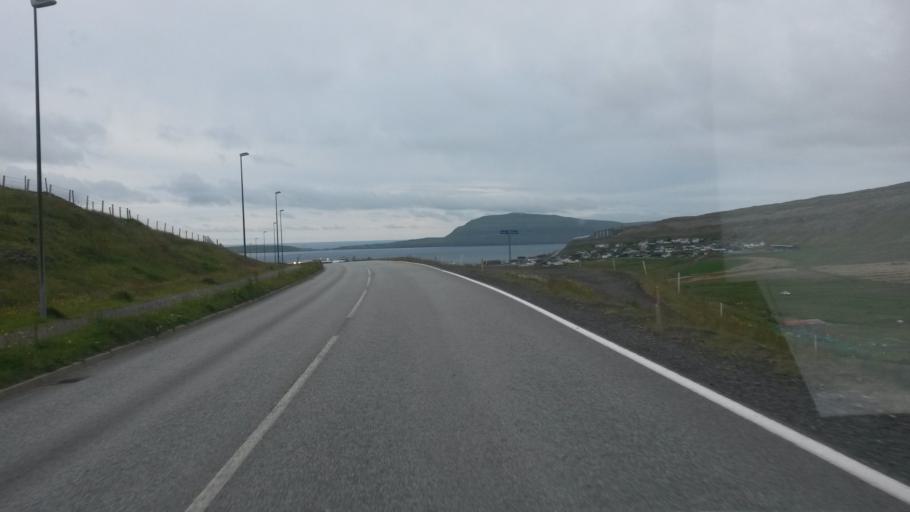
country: FO
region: Streymoy
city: Argir
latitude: 61.9987
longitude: -6.8200
